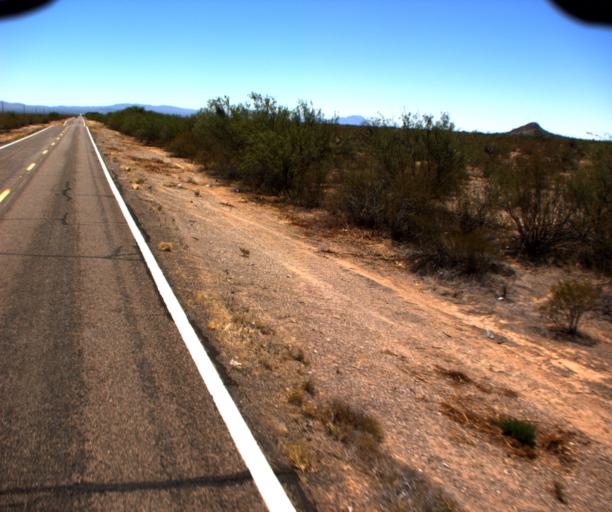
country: US
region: Arizona
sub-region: Pima County
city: Ajo
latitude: 32.2022
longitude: -112.5114
